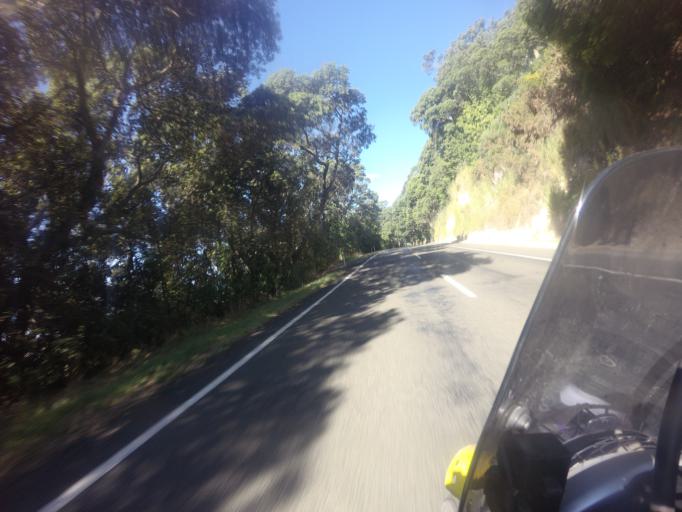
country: NZ
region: Bay of Plenty
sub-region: Opotiki District
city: Opotiki
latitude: -37.9918
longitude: 177.2299
